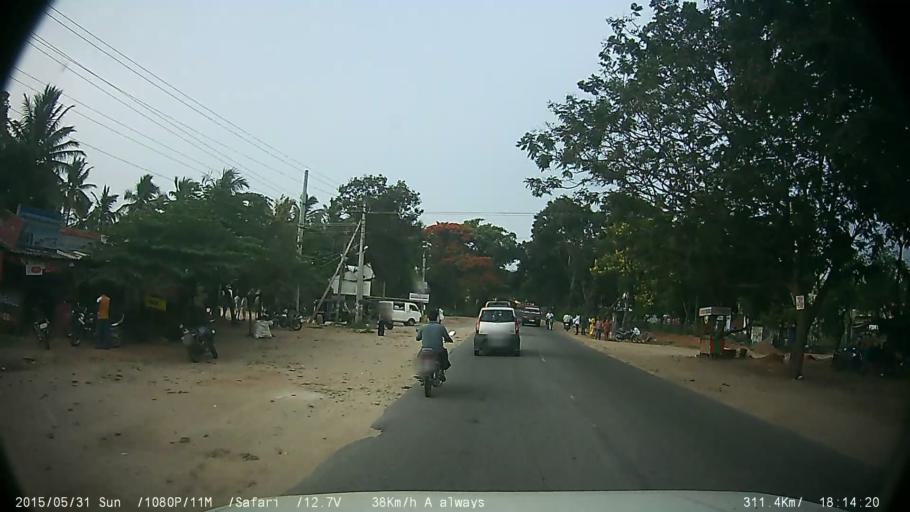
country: IN
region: Karnataka
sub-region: Mysore
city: Nanjangud
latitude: 12.1065
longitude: 76.6725
